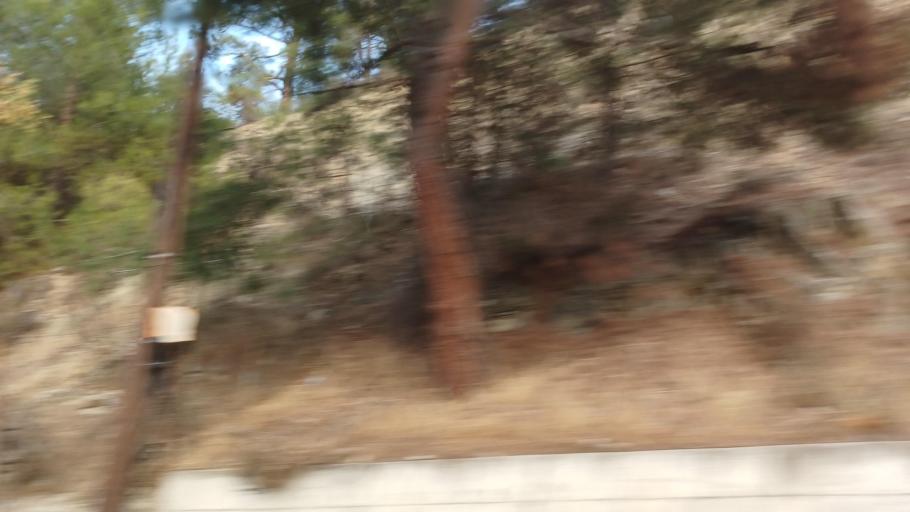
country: CY
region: Lefkosia
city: Kakopetria
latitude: 34.9723
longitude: 32.9196
